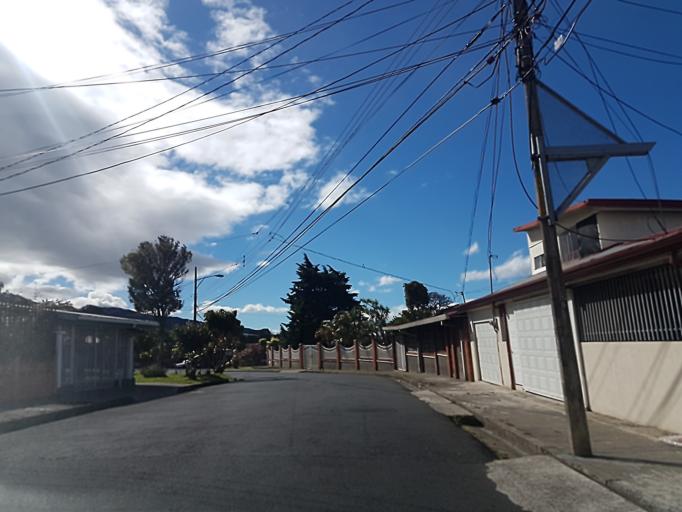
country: CR
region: San Jose
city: San Felipe
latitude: 9.9223
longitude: -84.0988
